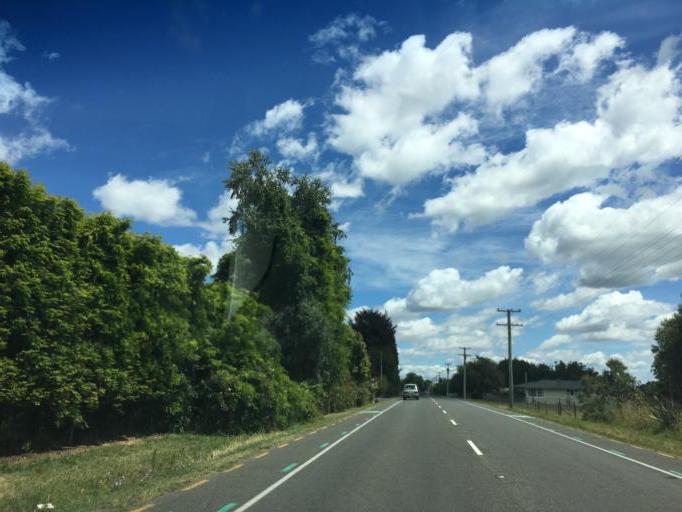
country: NZ
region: Hawke's Bay
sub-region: Hastings District
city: Hastings
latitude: -39.6553
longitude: 176.8712
